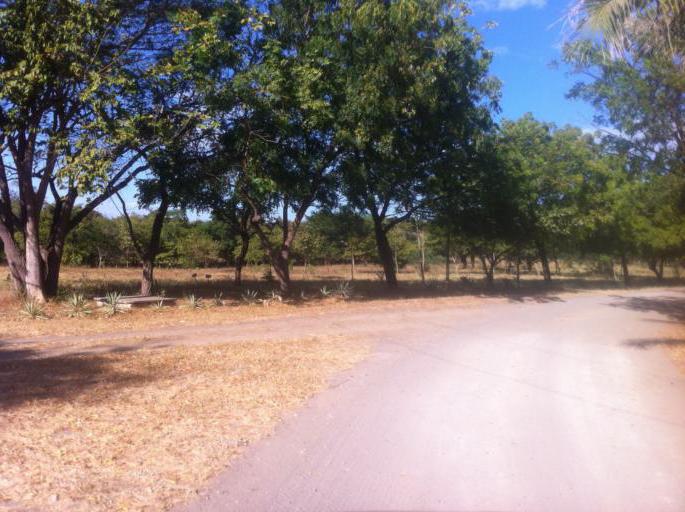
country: NI
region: Managua
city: Carlos Fonseca Amador
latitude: 11.9040
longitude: -86.6082
